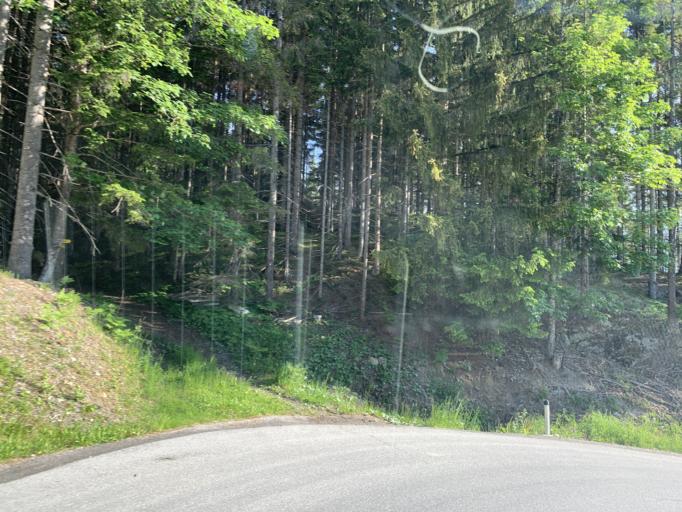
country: AT
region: Styria
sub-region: Politischer Bezirk Liezen
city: Schladming
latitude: 47.3765
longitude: 13.6108
